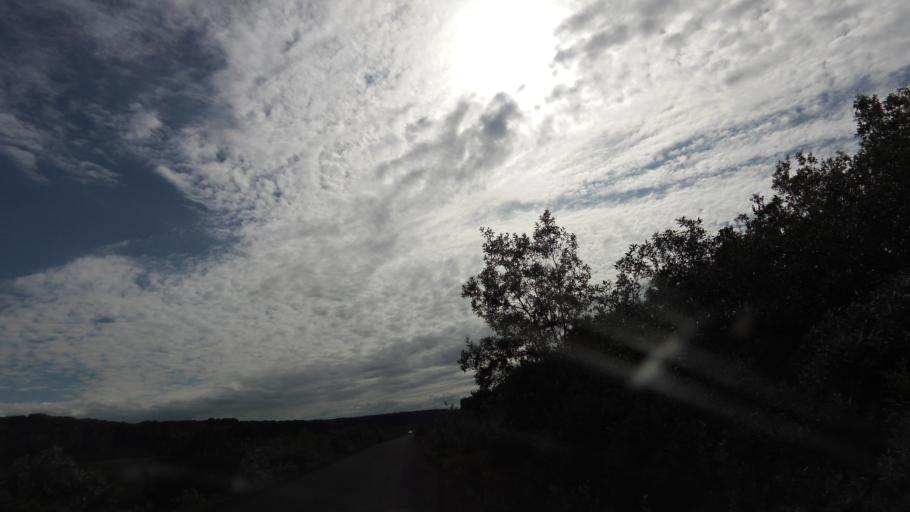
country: IS
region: Northeast
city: Husavik
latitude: 66.0240
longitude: -16.4946
